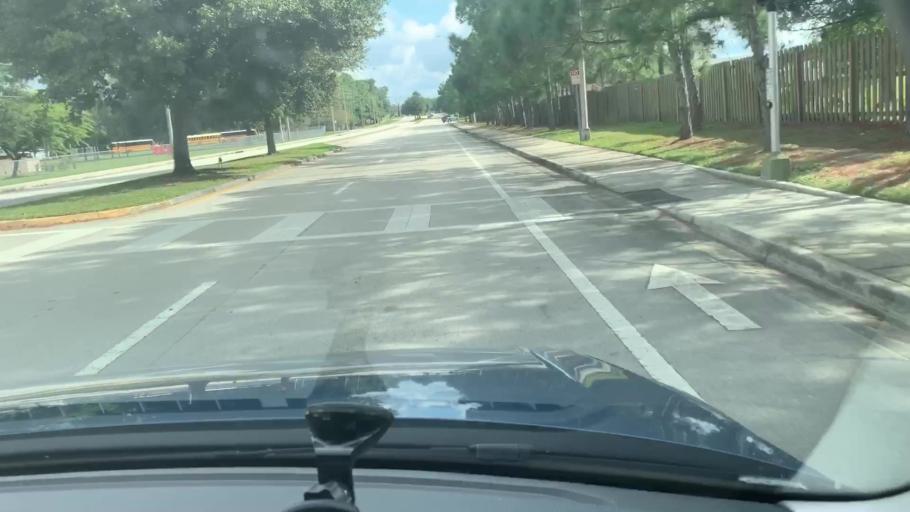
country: US
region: Florida
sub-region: Polk County
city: Gibsonia
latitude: 28.0915
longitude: -81.9925
